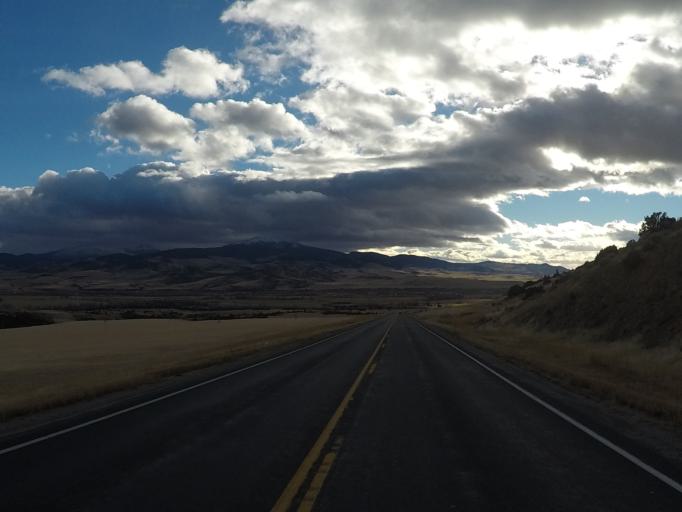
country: US
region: Montana
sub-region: Jefferson County
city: Whitehall
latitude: 45.8881
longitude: -111.9676
